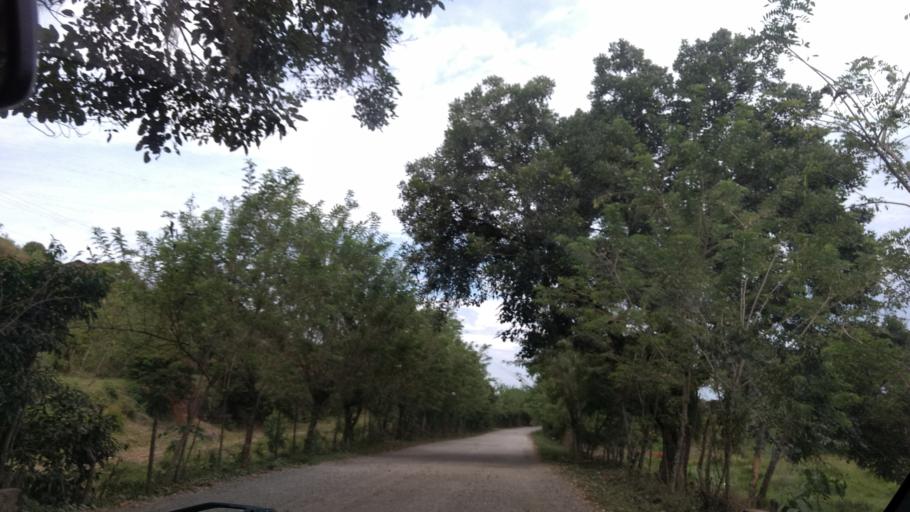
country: CO
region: Cauca
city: Buenos Aires
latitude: 3.0788
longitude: -76.6492
